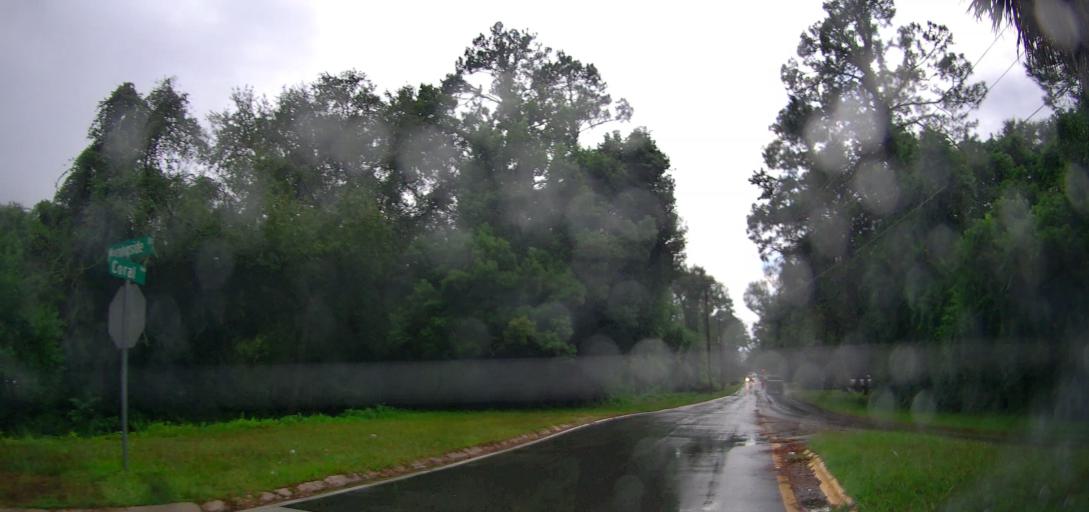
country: US
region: Georgia
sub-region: Ware County
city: Sunnyside
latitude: 31.2246
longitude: -82.3271
